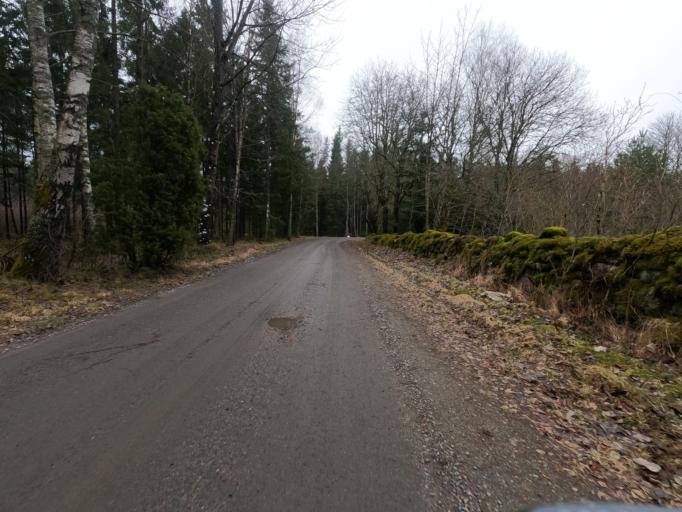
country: SE
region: Kronoberg
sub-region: Markaryds Kommun
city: Stromsnasbruk
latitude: 56.8102
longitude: 13.5667
